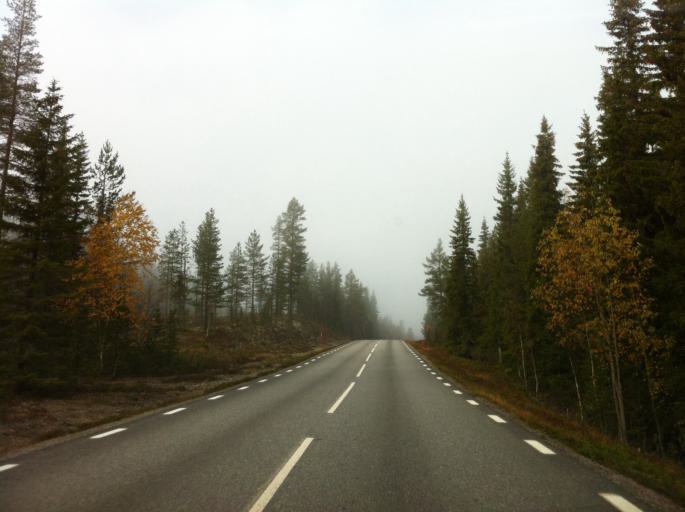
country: NO
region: Hedmark
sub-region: Engerdal
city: Engerdal
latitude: 61.9779
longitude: 12.4902
